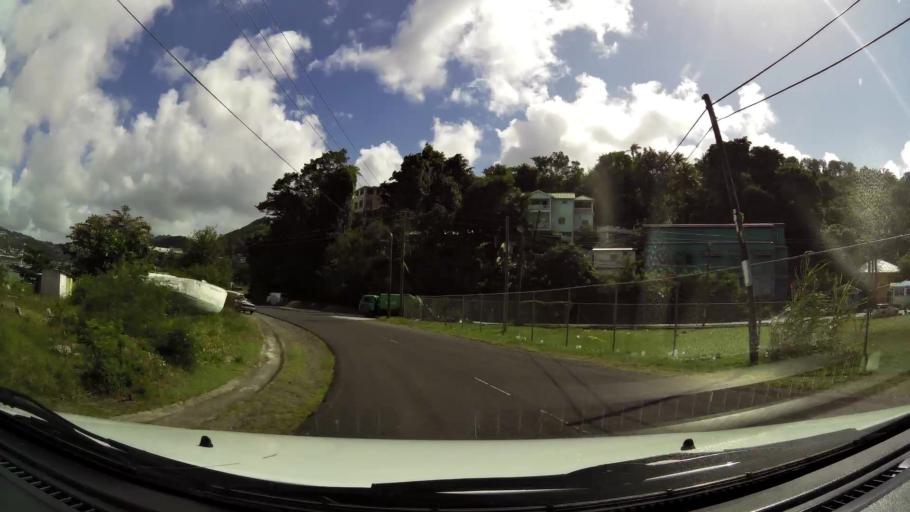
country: LC
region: Castries Quarter
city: Castries
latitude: 14.0121
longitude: -61.0026
